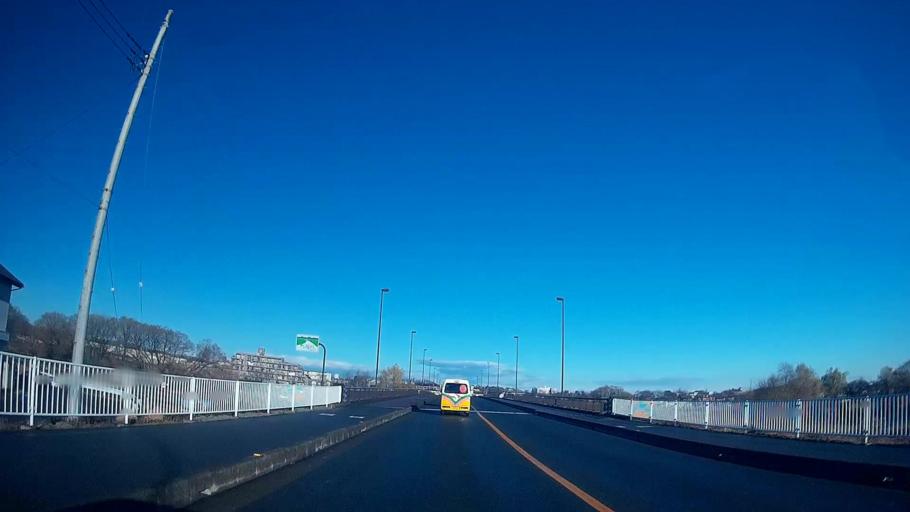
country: JP
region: Saitama
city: Sayama
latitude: 35.8497
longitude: 139.3836
